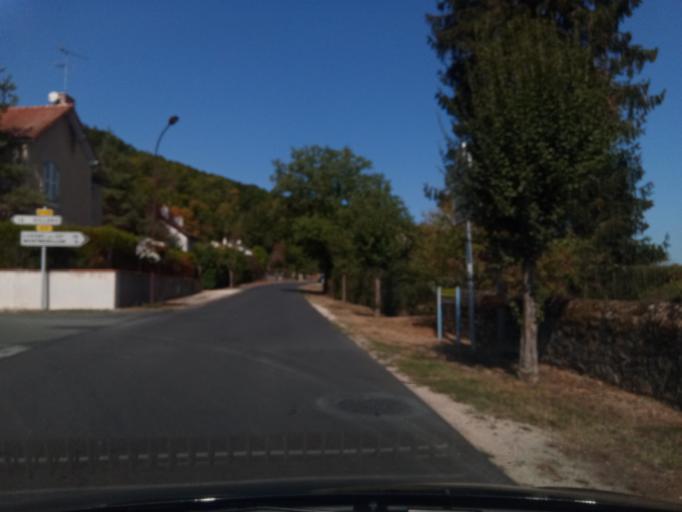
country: FR
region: Poitou-Charentes
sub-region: Departement de la Vienne
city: Saulge
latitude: 46.3792
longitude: 0.8733
